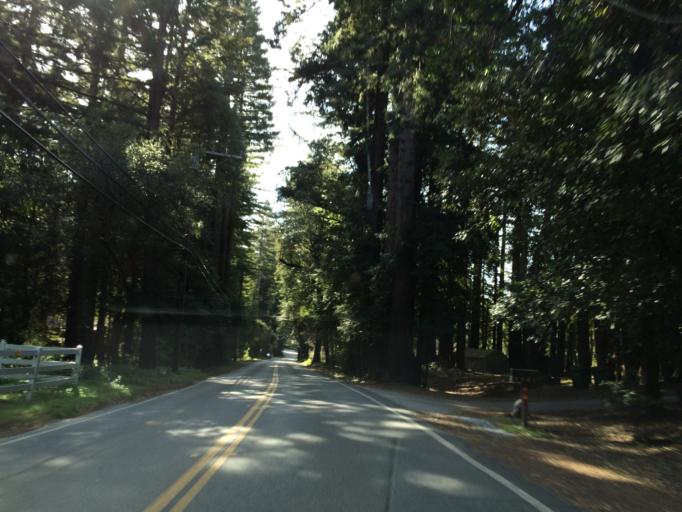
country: US
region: California
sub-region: Santa Cruz County
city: Bonny Doon
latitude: 37.0758
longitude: -122.1314
